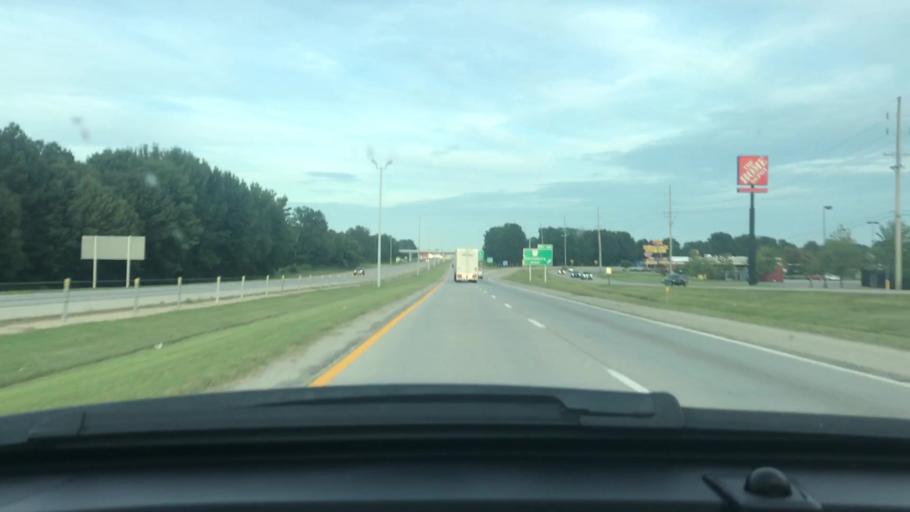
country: US
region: Arkansas
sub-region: Craighead County
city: Jonesboro
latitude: 35.8072
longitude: -90.7052
